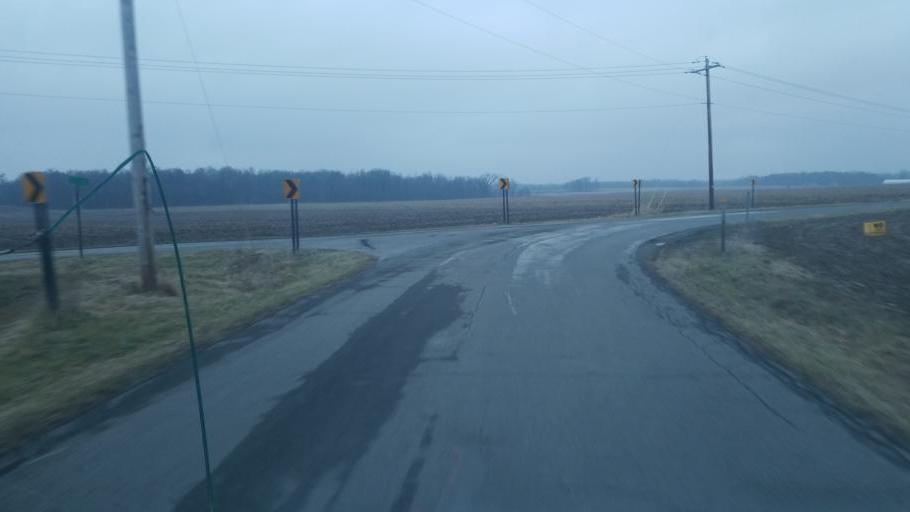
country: US
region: Ohio
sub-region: Seneca County
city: Tiffin
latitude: 41.0004
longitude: -83.1476
